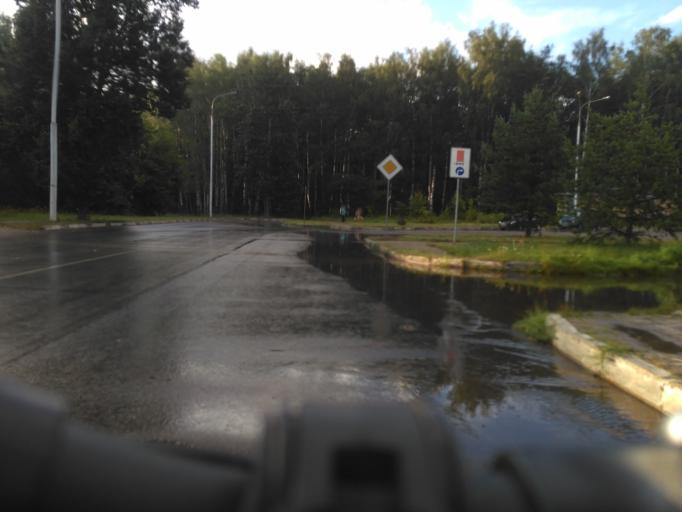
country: RU
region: Moskovskaya
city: Dubna
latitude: 56.7525
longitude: 37.2028
